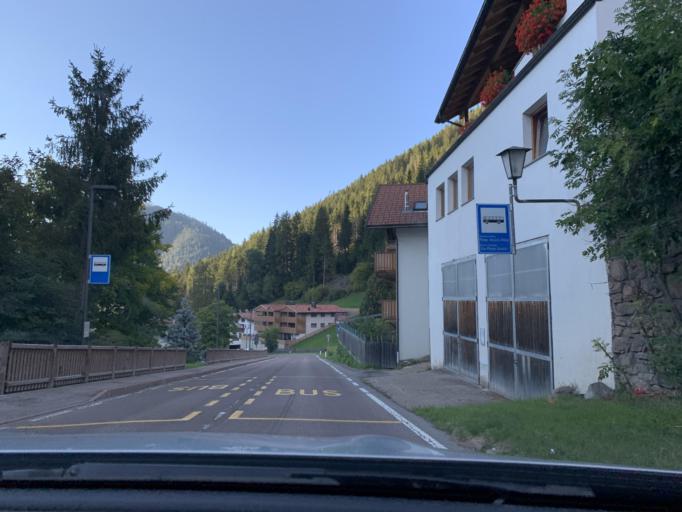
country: IT
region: Trentino-Alto Adige
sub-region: Bolzano
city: Nova Levante
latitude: 46.4228
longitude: 11.5556
